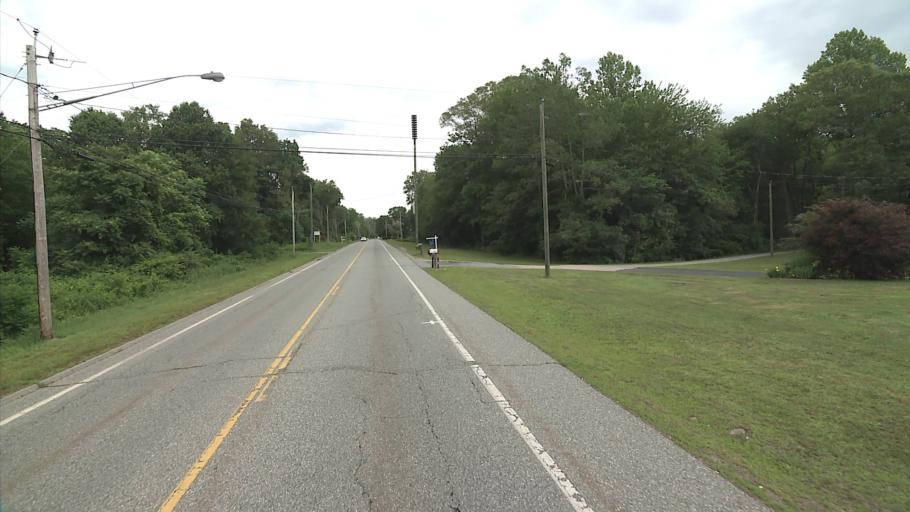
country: US
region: Connecticut
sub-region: New London County
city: Conning Towers-Nautilus Park
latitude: 41.3956
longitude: -72.0272
